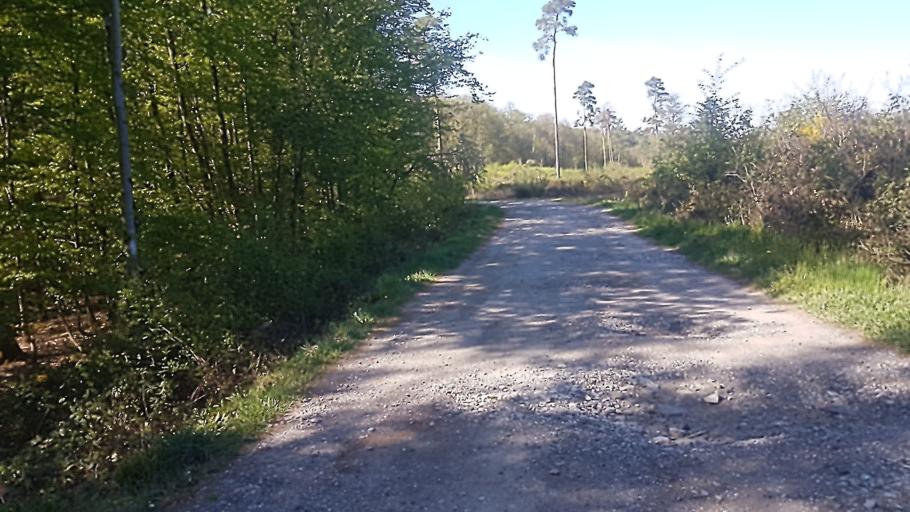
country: BE
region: Wallonia
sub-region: Province de Namur
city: Couvin
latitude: 50.0665
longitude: 4.5912
